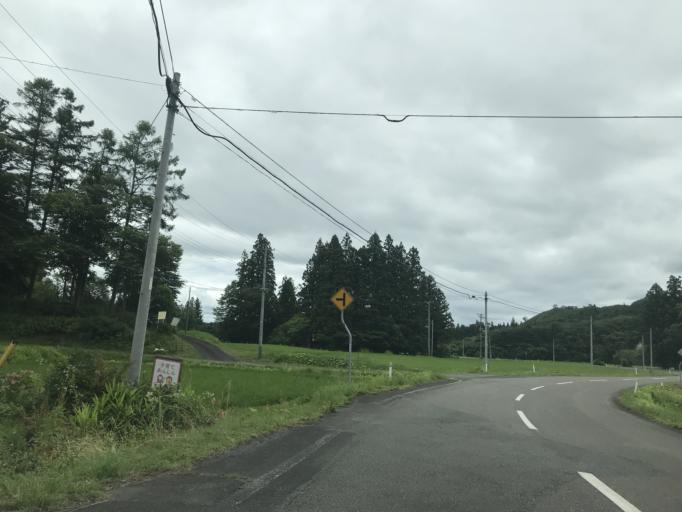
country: JP
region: Iwate
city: Ichinoseki
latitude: 38.9560
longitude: 140.9371
